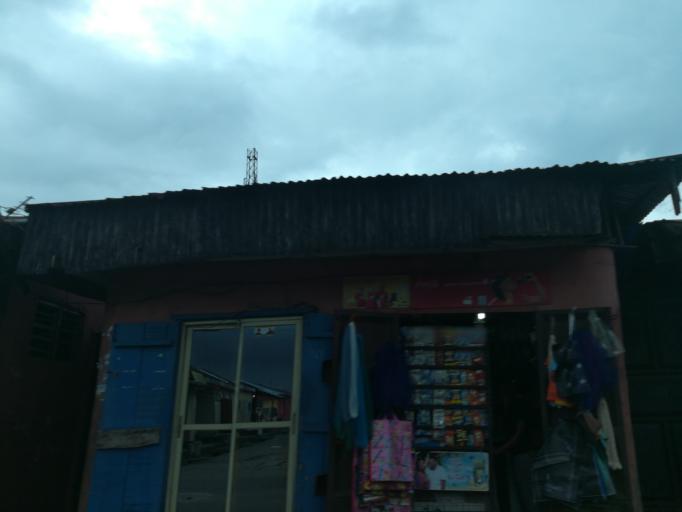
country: NG
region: Rivers
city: Port Harcourt
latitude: 4.8032
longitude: 6.9887
